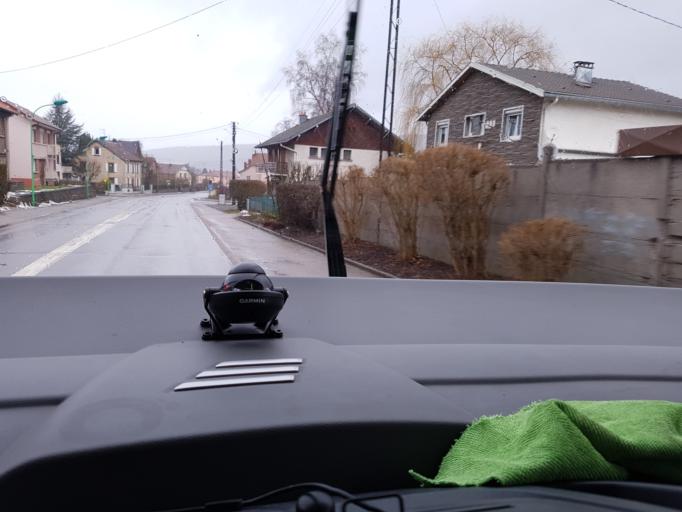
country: FR
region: Lorraine
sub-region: Departement des Vosges
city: Fraize
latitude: 48.1805
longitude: 7.0062
